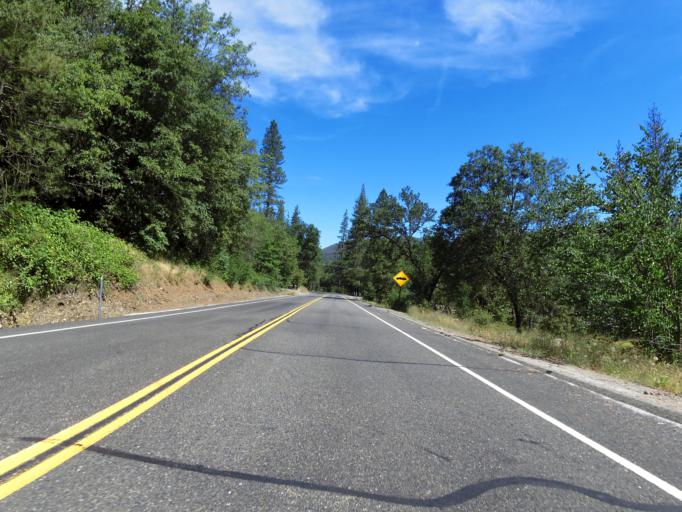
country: US
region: California
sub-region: Mariposa County
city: Midpines
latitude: 37.5454
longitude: -119.9205
